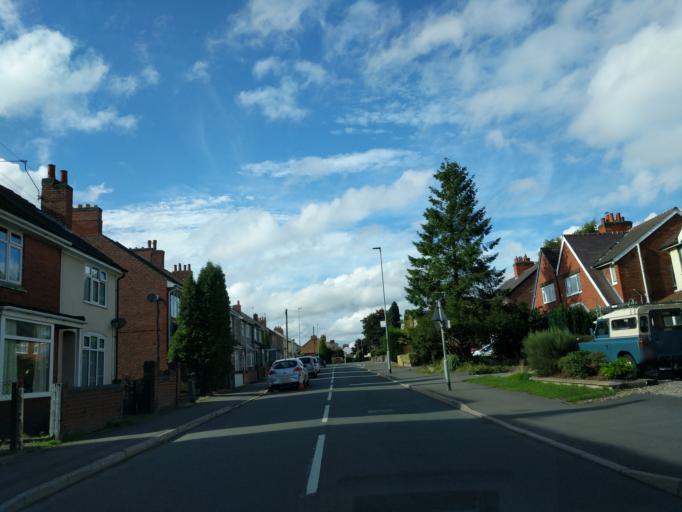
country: GB
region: England
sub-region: Leicestershire
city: Coalville
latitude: 52.7117
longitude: -1.3789
